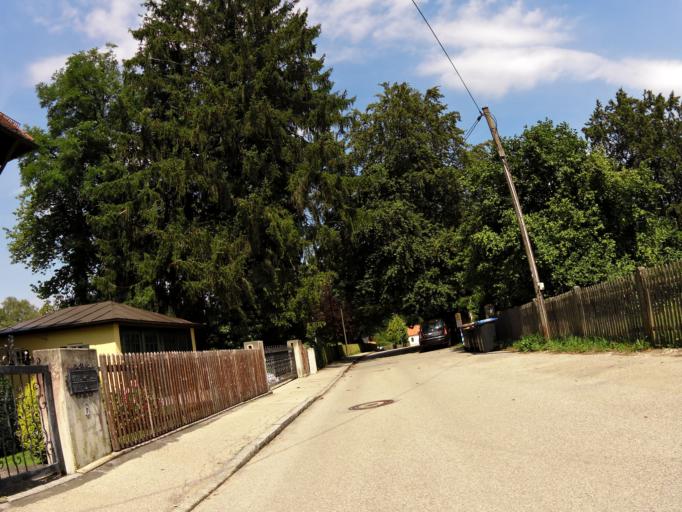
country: DE
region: Bavaria
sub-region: Upper Bavaria
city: Inning am Ammersee
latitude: 48.0547
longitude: 11.1364
